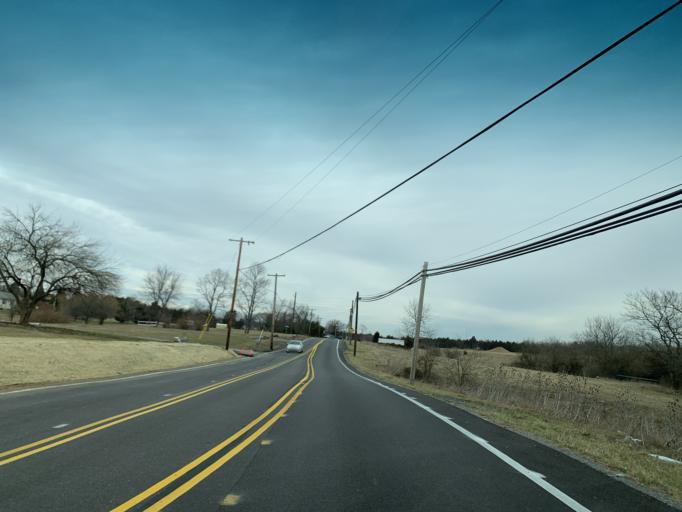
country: US
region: Maryland
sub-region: Washington County
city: Williamsport
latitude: 39.5472
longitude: -77.9017
